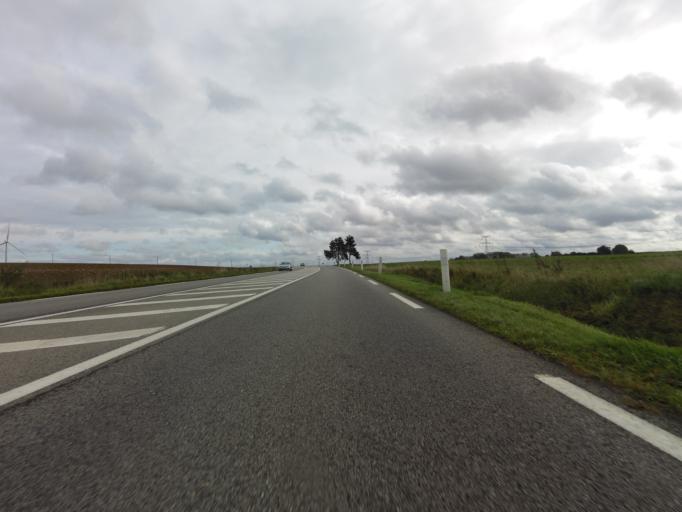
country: FR
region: Haute-Normandie
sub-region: Departement de la Seine-Maritime
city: Criel-sur-Mer
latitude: 50.0185
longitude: 1.3575
